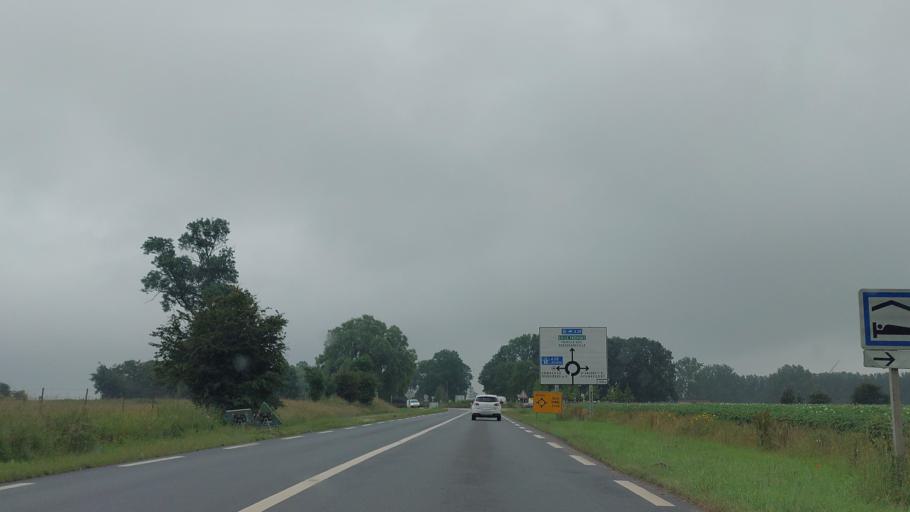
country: FR
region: Picardie
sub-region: Departement de la Somme
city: Feuquieres-en-Vimeu
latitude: 50.0774
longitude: 1.6131
